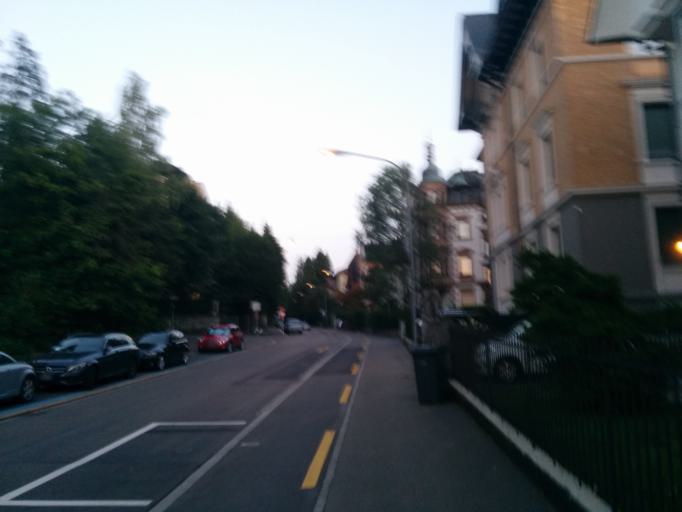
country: CH
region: Zurich
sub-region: Bezirk Zuerich
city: Zuerich (Kreis 7) / Hottingen
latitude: 47.3655
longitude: 8.5599
